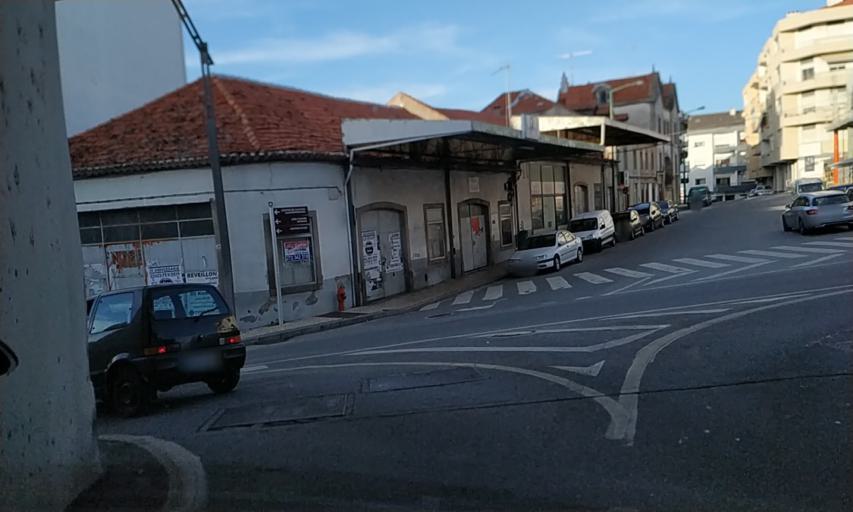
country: PT
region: Castelo Branco
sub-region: Castelo Branco
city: Castelo Branco
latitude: 39.8230
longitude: -7.4889
